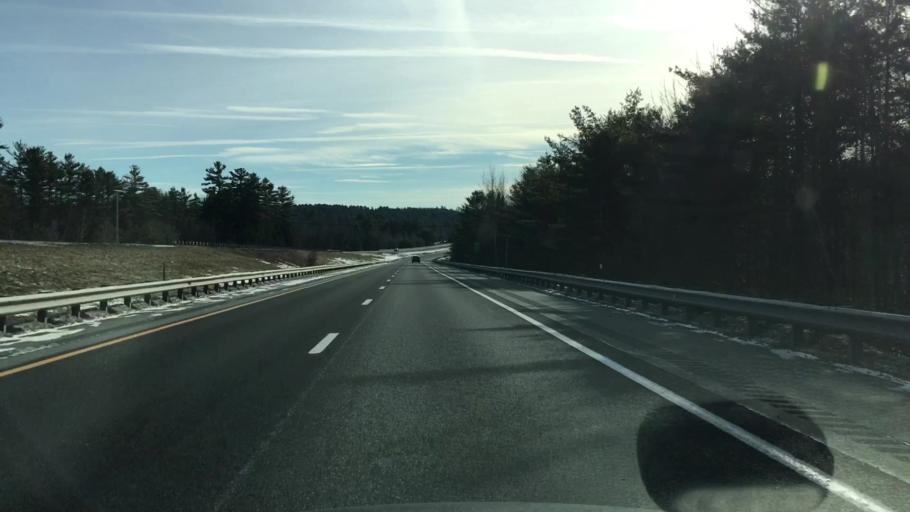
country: US
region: New Hampshire
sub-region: Sullivan County
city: Grantham
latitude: 43.5443
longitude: -72.1392
